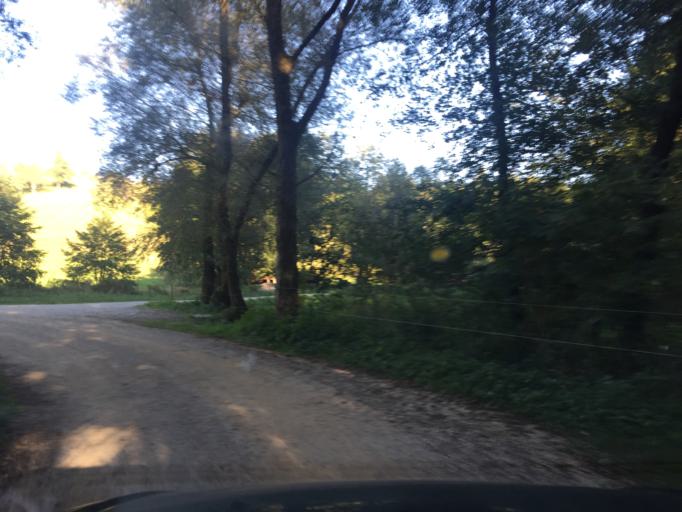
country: SI
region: Postojna
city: Postojna
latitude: 45.8120
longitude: 14.1299
